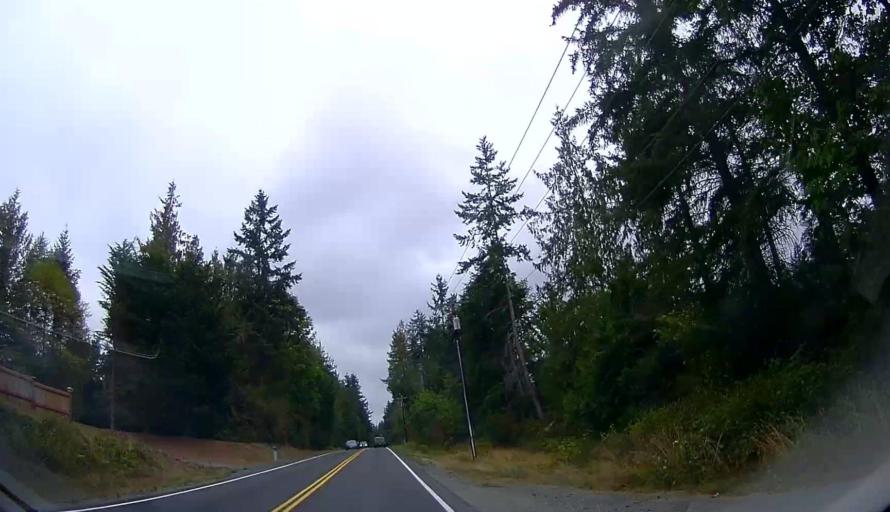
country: US
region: Washington
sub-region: Snohomish County
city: Warm Beach
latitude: 48.1711
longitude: -122.3560
